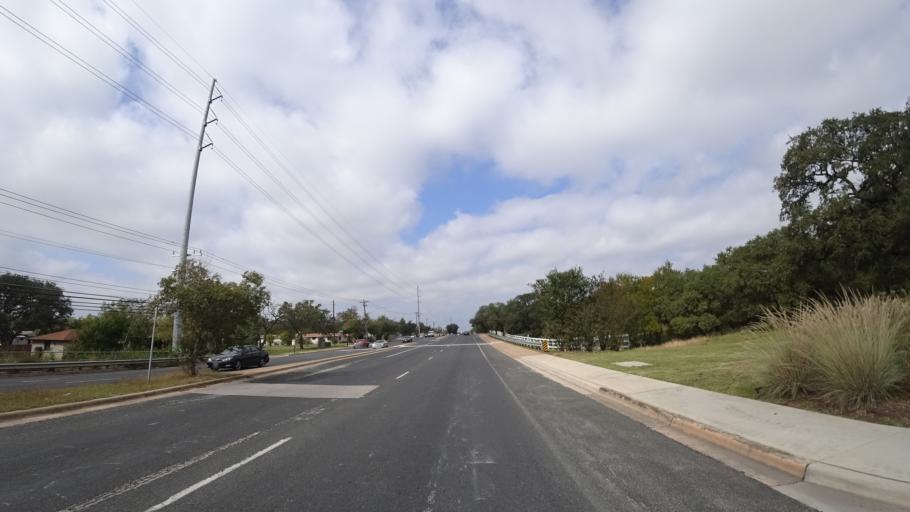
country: US
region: Texas
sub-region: Travis County
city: Shady Hollow
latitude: 30.1811
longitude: -97.8446
